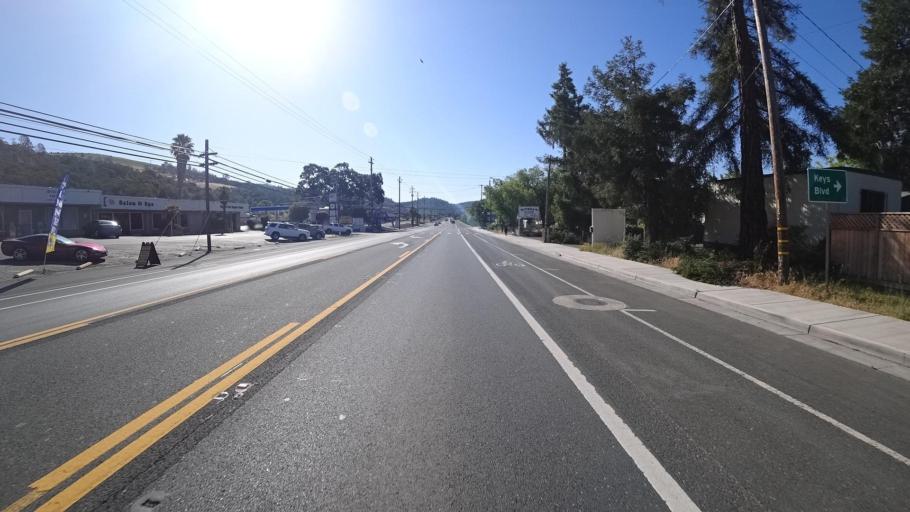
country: US
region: California
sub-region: Lake County
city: Clearlake Oaks
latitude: 39.0259
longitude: -122.6612
